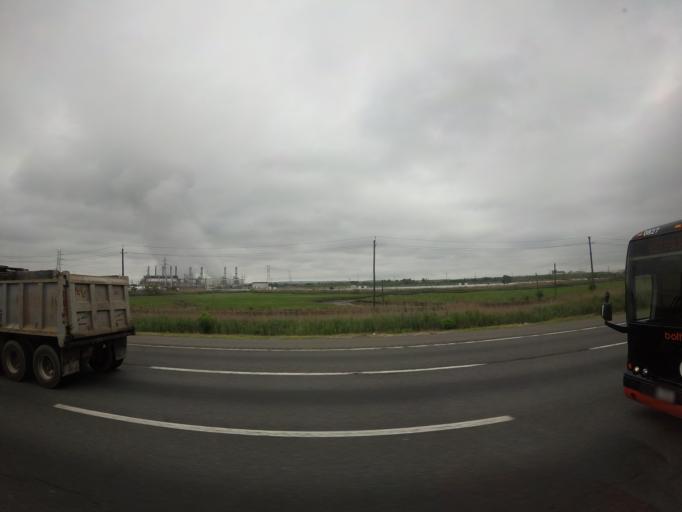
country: US
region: New Jersey
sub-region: Union County
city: Linden
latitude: 40.6211
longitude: -74.2180
